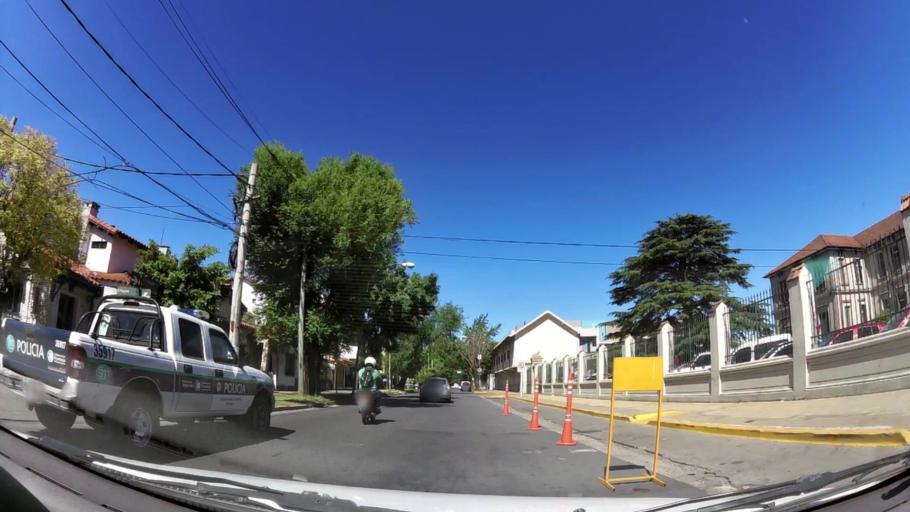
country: AR
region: Buenos Aires
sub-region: Partido de Vicente Lopez
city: Olivos
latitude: -34.5277
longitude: -58.4990
